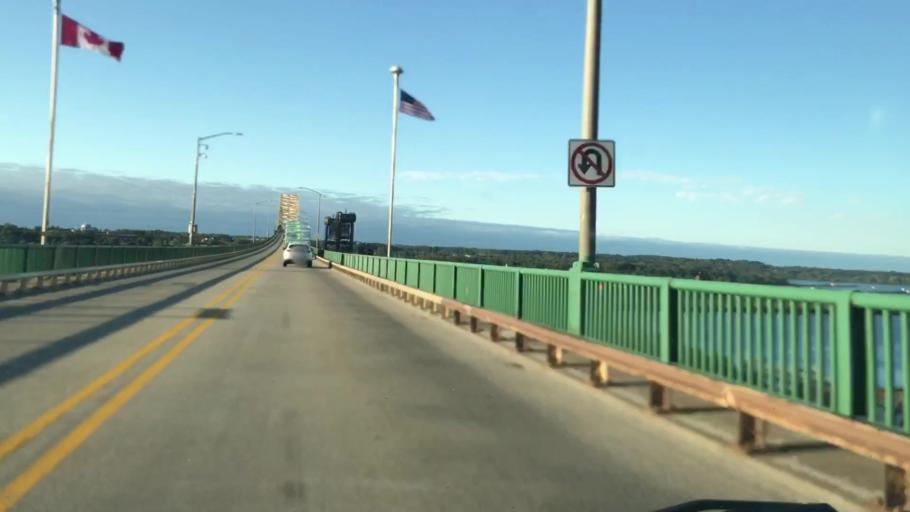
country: US
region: Michigan
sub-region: Chippewa County
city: Sault Ste. Marie
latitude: 46.5085
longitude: -84.3607
